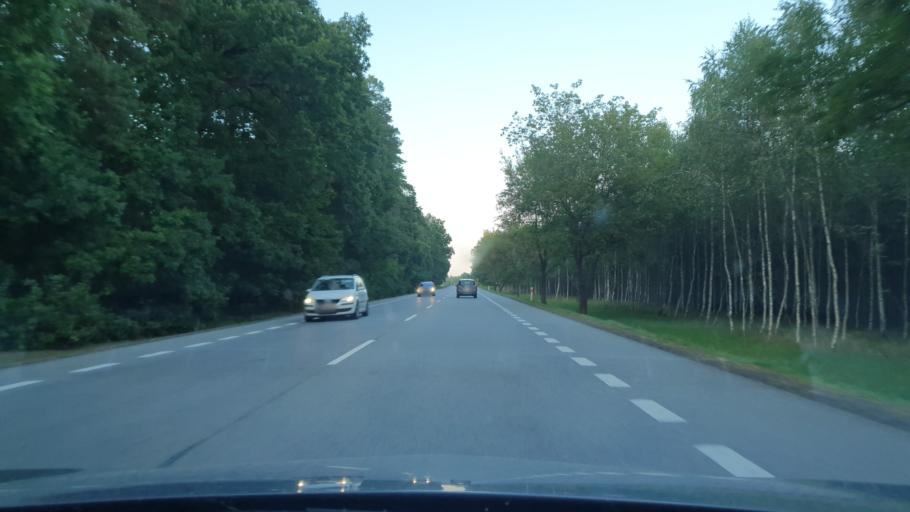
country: PL
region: Pomeranian Voivodeship
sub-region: Powiat leborski
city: Nowa Wies Leborska
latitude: 54.4964
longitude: 17.6181
